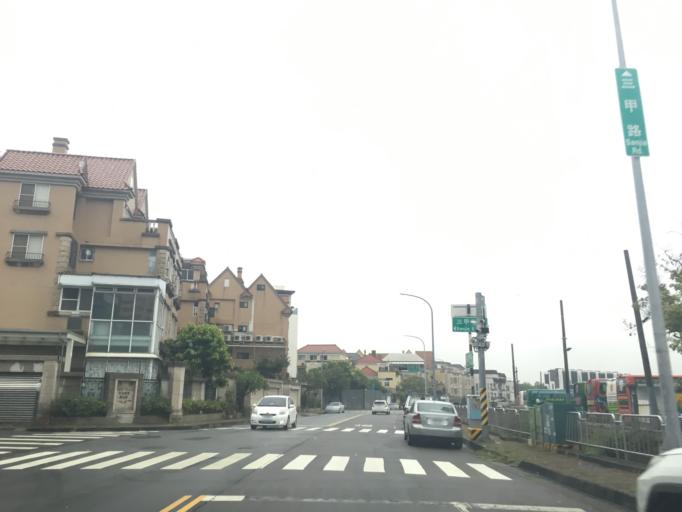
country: TW
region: Taiwan
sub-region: Taichung City
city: Taichung
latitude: 24.1712
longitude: 120.7142
